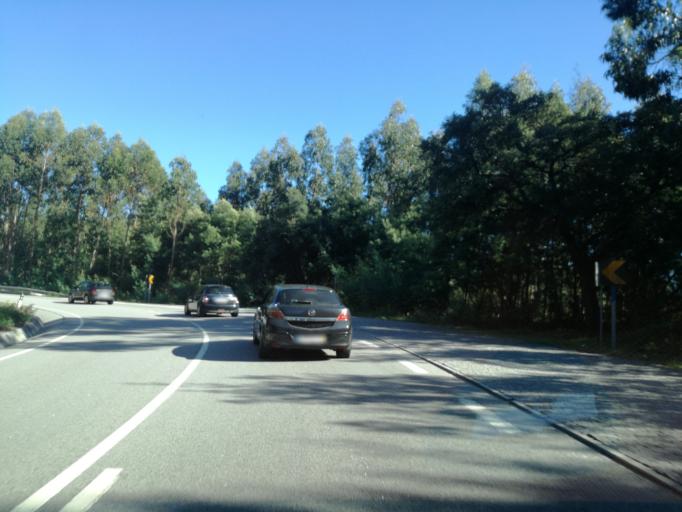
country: PT
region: Porto
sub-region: Pacos de Ferreira
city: Seroa
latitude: 41.2572
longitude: -8.4559
